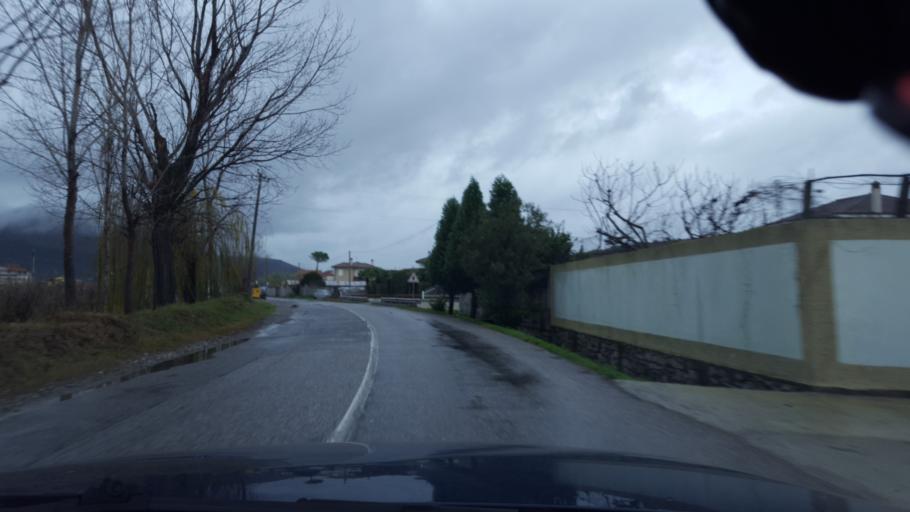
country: AL
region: Shkoder
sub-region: Rrethi i Shkodres
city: Berdica e Madhe
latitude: 42.0081
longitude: 19.4807
